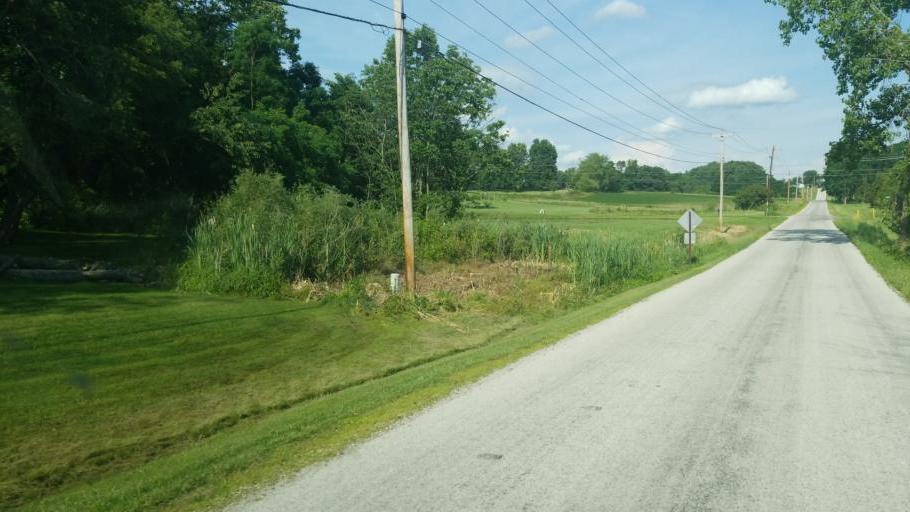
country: US
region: Ohio
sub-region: Richland County
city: Lexington
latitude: 40.6445
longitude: -82.6109
